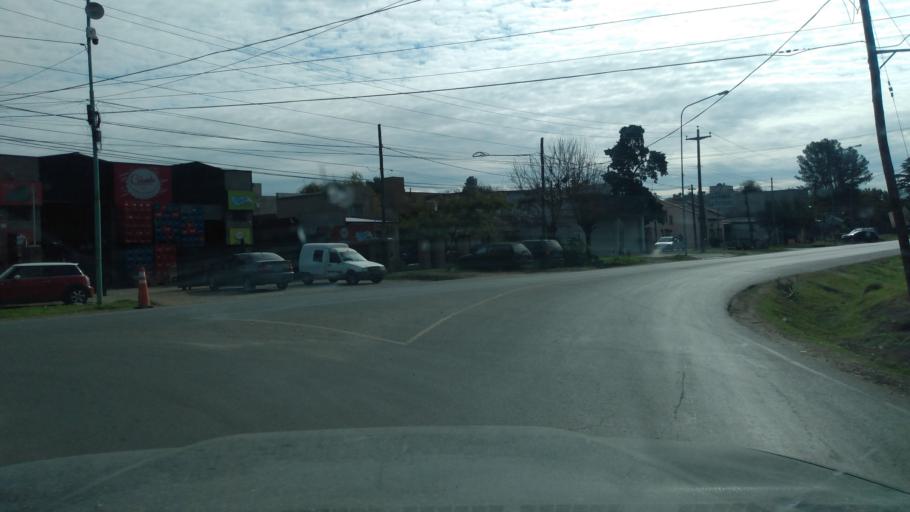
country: AR
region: Buenos Aires
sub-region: Partido de Lujan
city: Lujan
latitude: -34.5554
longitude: -59.1256
